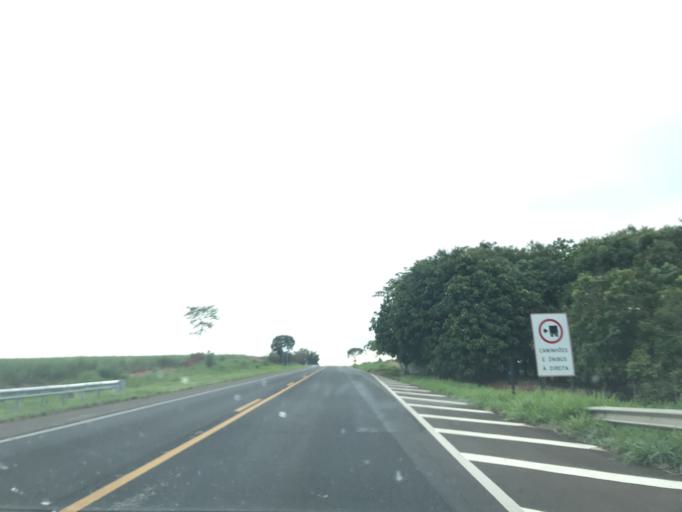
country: BR
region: Sao Paulo
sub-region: Penapolis
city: Penapolis
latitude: -21.4960
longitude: -50.2427
